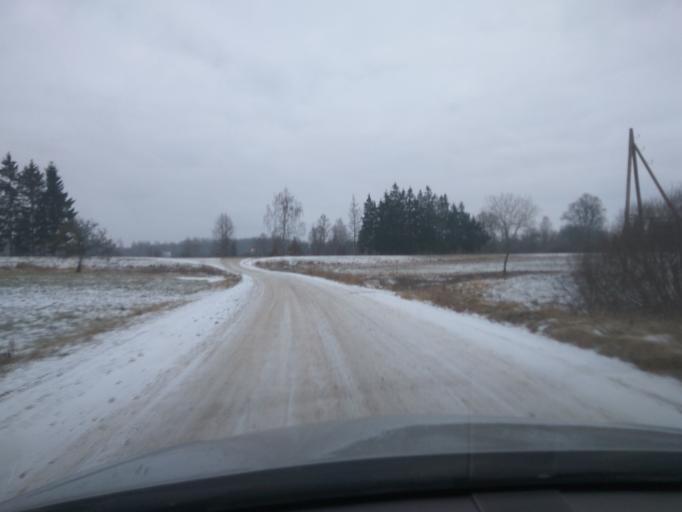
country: LV
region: Aizpute
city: Aizpute
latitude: 56.7331
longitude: 21.6666
